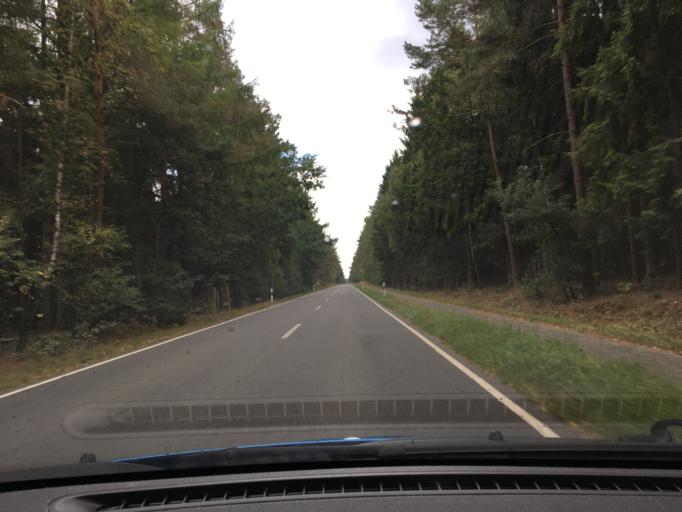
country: DE
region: Lower Saxony
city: Jesteburg
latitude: 53.2613
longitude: 9.9113
